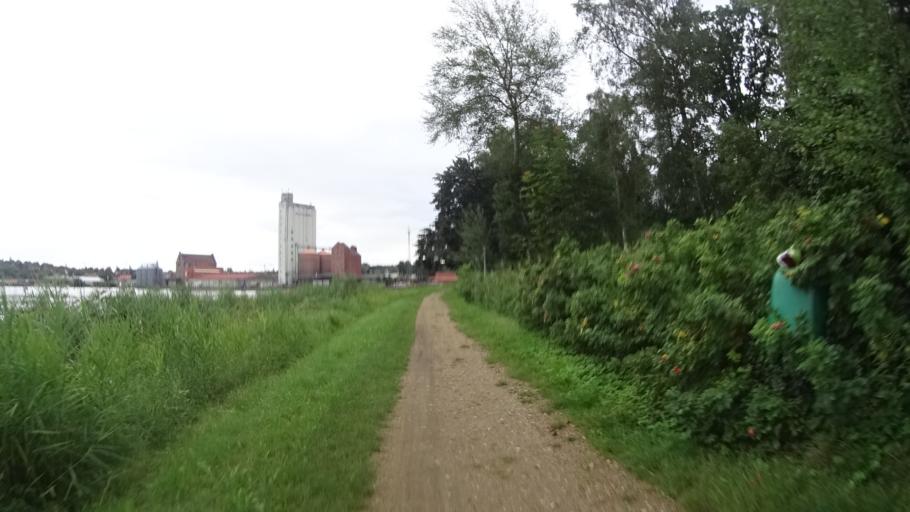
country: DE
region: Schleswig-Holstein
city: Molln
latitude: 53.6277
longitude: 10.6726
